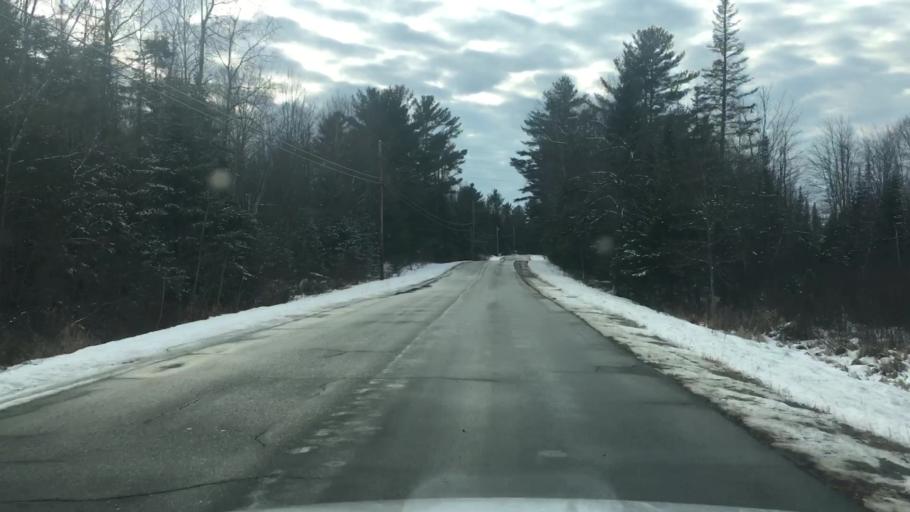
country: US
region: Maine
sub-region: Kennebec County
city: Chelsea
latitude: 44.2826
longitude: -69.6683
